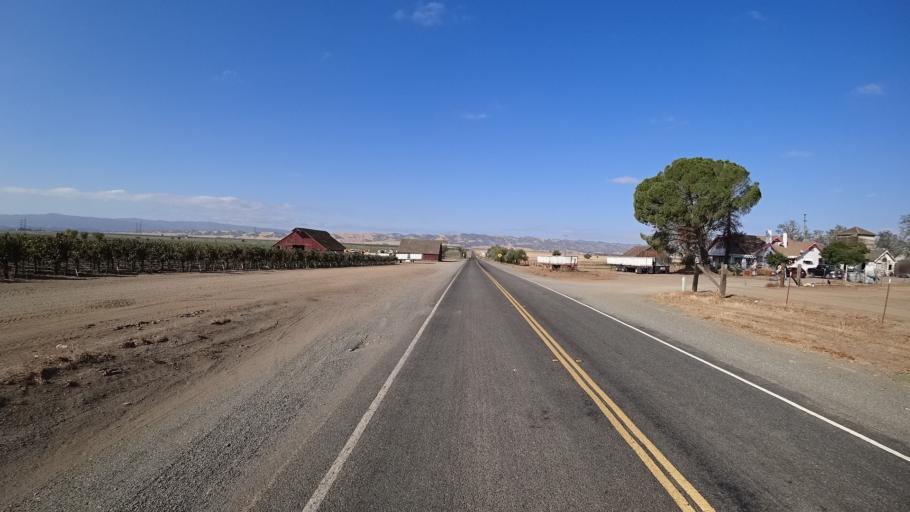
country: US
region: California
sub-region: Yolo County
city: Esparto
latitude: 38.7808
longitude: -122.0042
